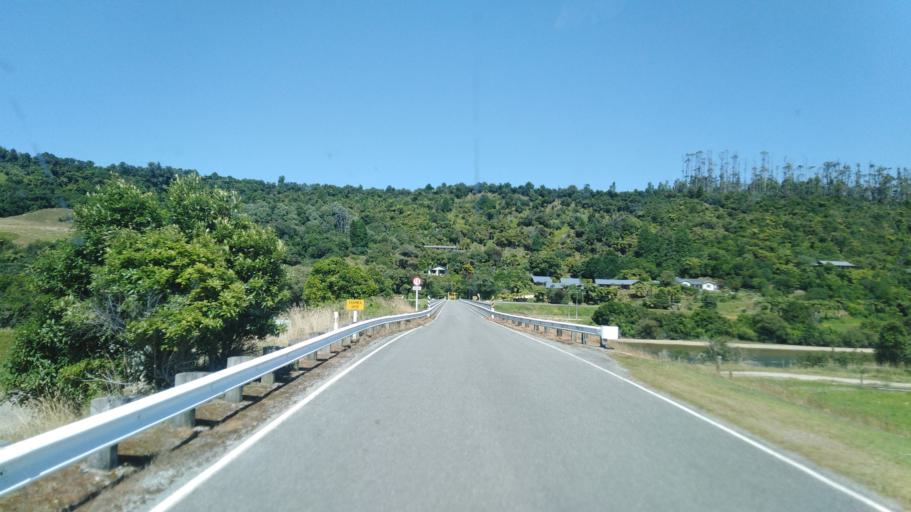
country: NZ
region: West Coast
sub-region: Buller District
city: Westport
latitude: -41.2601
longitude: 172.1321
